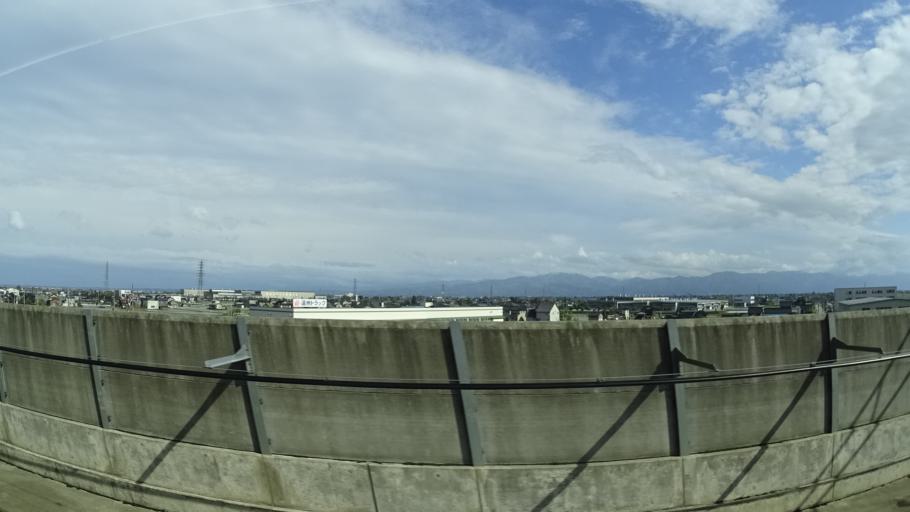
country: JP
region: Toyama
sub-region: Oyabe Shi
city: Oyabe
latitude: 36.6968
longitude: 136.9331
